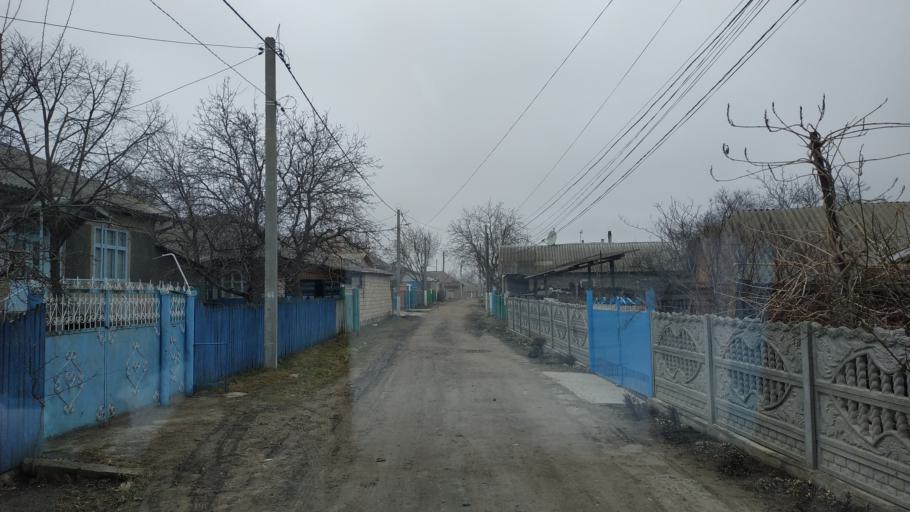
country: MD
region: Hincesti
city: Hincesti
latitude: 46.8927
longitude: 28.5463
